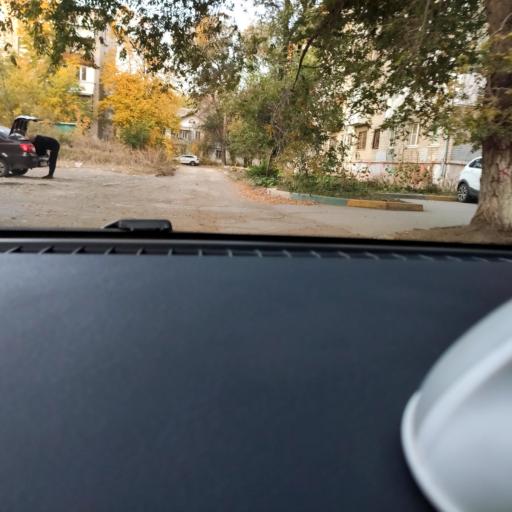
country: RU
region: Samara
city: Samara
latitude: 53.2126
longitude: 50.2336
